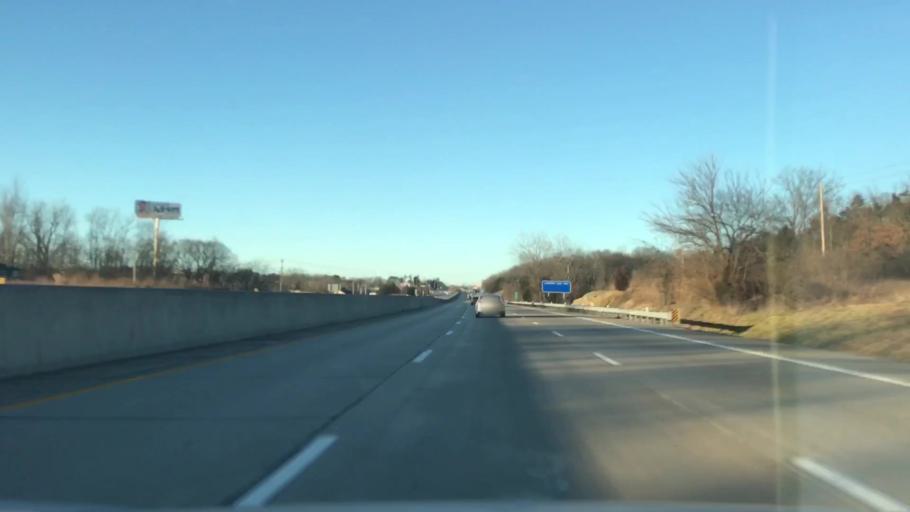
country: US
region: Missouri
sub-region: Franklin County
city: Gray Summit
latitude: 38.4872
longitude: -90.8080
